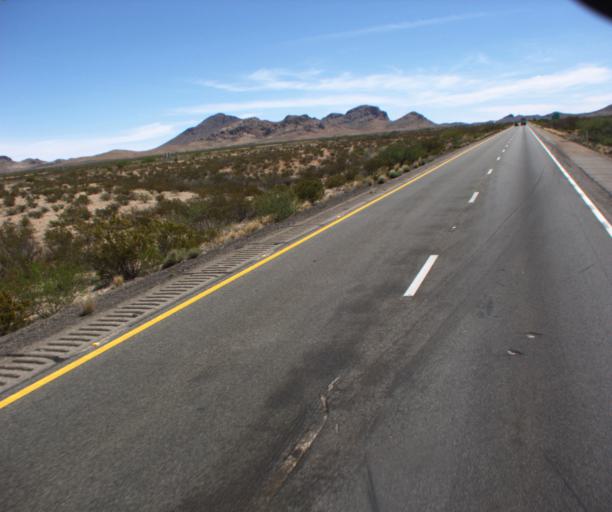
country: US
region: New Mexico
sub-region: Hidalgo County
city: Lordsburg
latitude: 32.2325
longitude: -109.0708
